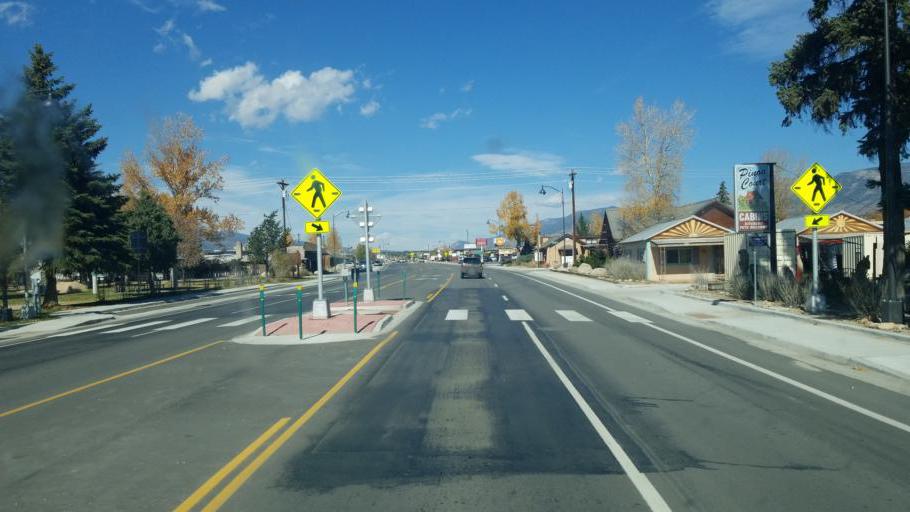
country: US
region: Colorado
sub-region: Chaffee County
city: Buena Vista
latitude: 38.8433
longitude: -106.1333
